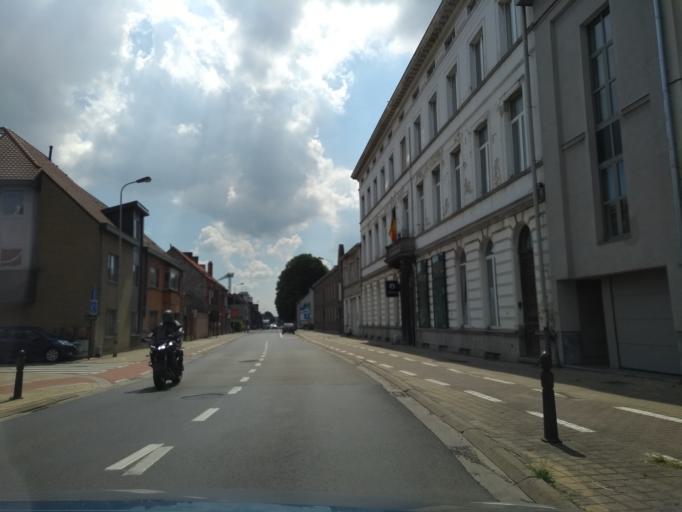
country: BE
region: Flanders
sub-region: Provincie Oost-Vlaanderen
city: Eeklo
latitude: 51.1857
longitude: 3.5576
